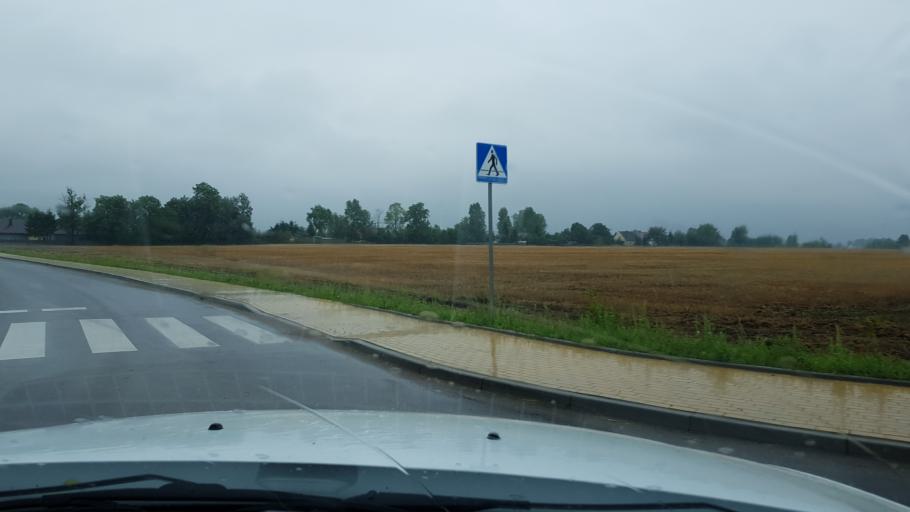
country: PL
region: West Pomeranian Voivodeship
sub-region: Powiat kolobrzeski
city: Ustronie Morskie
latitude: 54.2140
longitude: 15.8455
